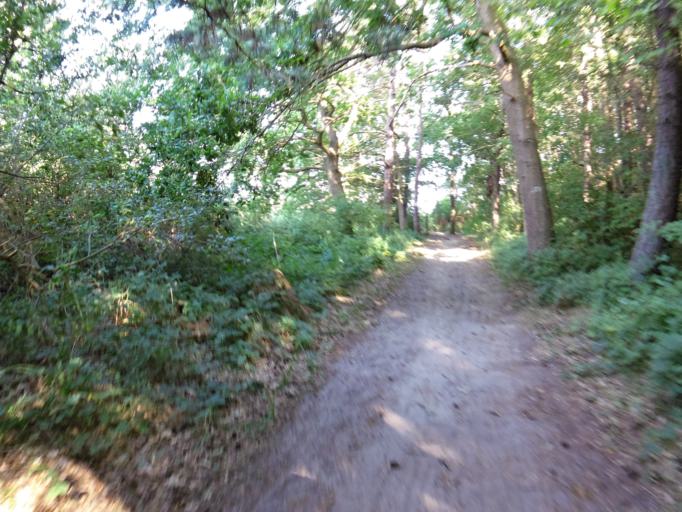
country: DE
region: Mecklenburg-Vorpommern
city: Loddin
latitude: 53.9675
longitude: 14.0433
